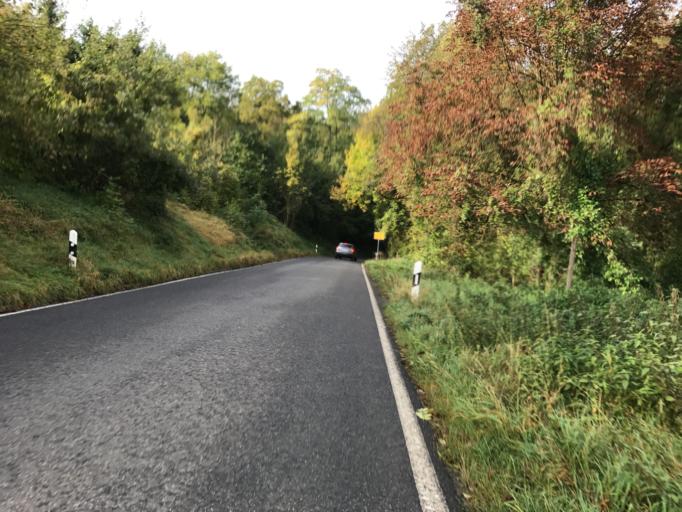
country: DE
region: Rheinland-Pfalz
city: Nieder-Hilbersheim
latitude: 49.9134
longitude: 8.0480
